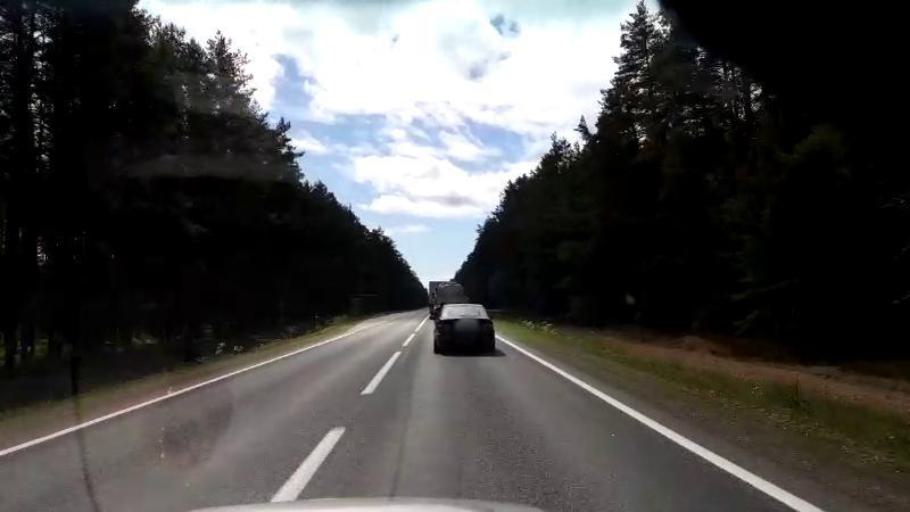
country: LV
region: Salacgrivas
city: Salacgriva
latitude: 57.5371
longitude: 24.4315
